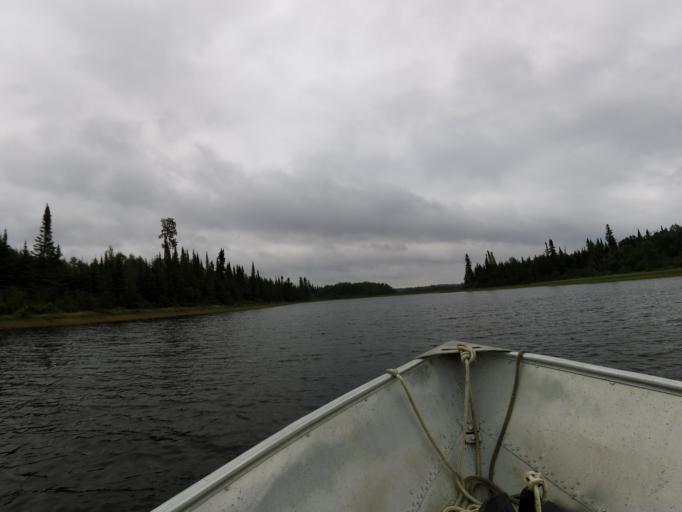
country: CA
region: Ontario
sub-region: Rainy River District
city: Atikokan
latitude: 49.5952
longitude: -91.3395
